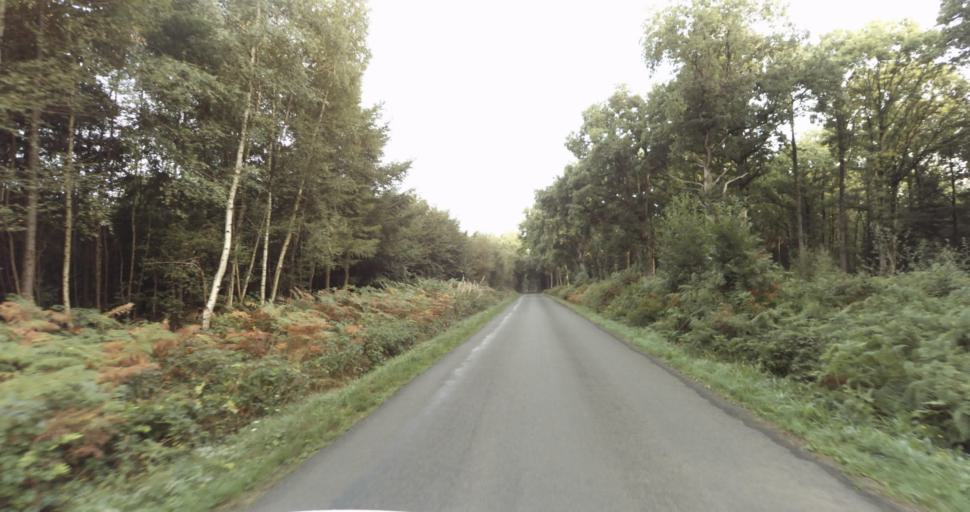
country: FR
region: Lower Normandy
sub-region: Departement de l'Orne
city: Vimoutiers
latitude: 48.9312
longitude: 0.2817
